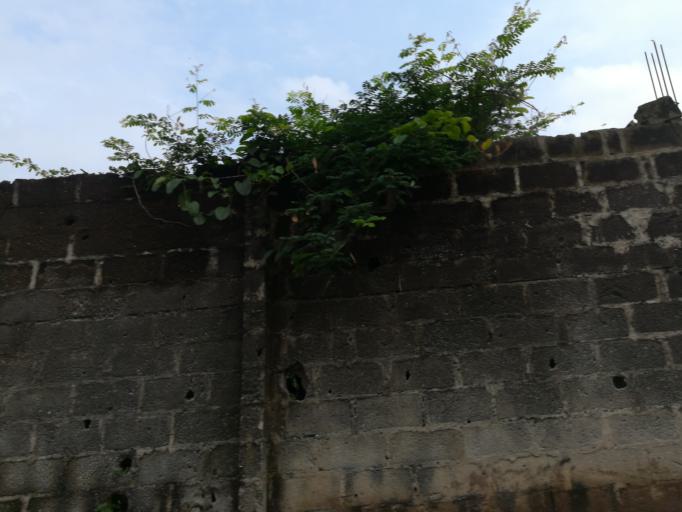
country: NG
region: Rivers
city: Port Harcourt
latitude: 4.8417
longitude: 7.0542
